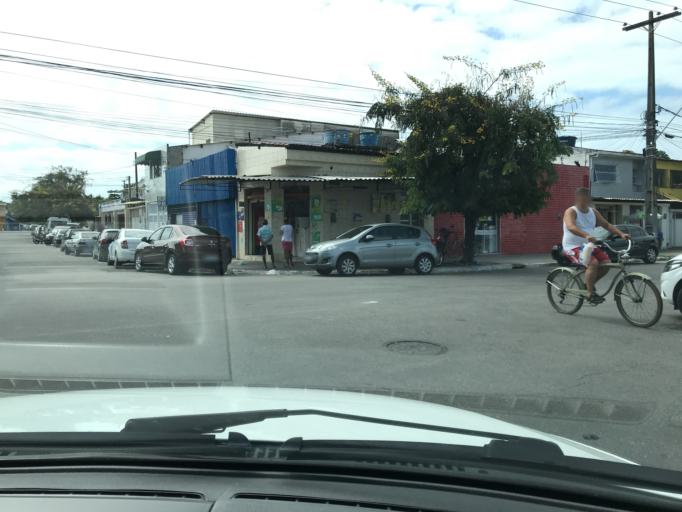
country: BR
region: Pernambuco
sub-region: Recife
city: Recife
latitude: -8.0451
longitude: -34.8825
